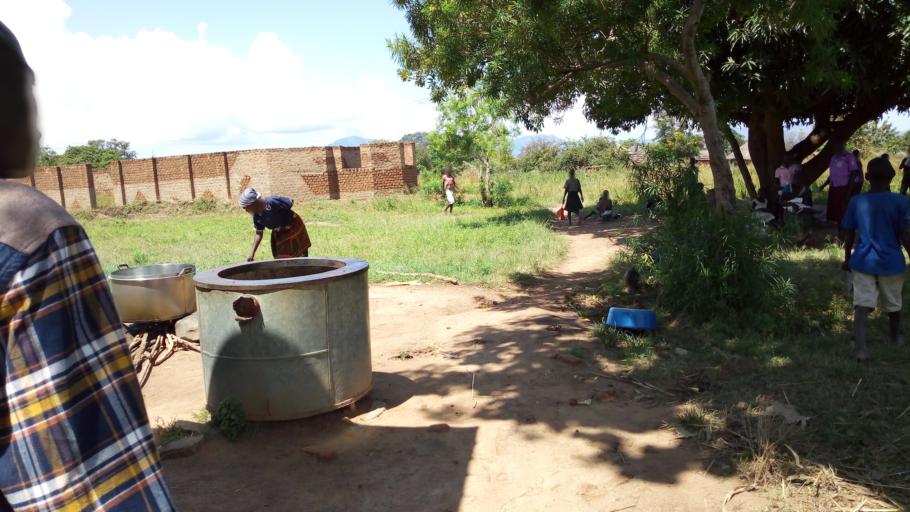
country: UG
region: Northern Region
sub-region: Adjumani District
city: Adjumani
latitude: 3.4576
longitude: 31.8953
